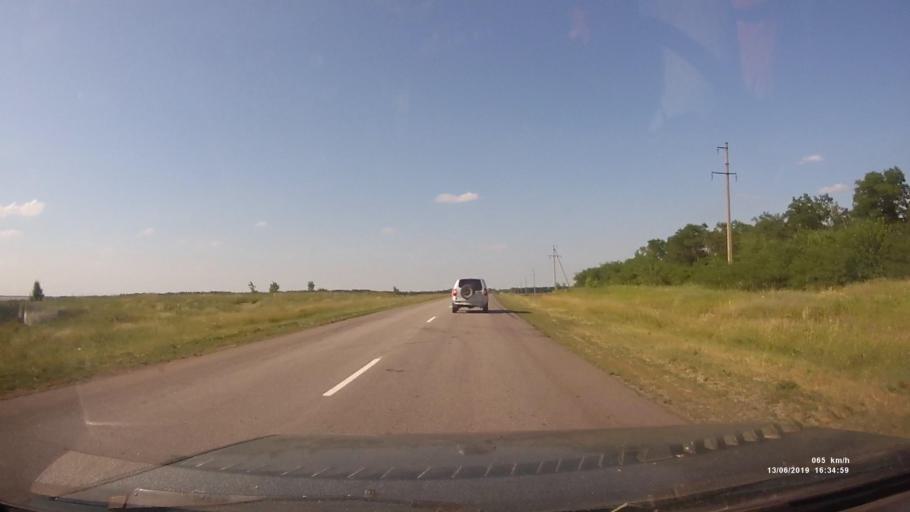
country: RU
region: Rostov
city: Kazanskaya
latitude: 49.8780
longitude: 41.2959
